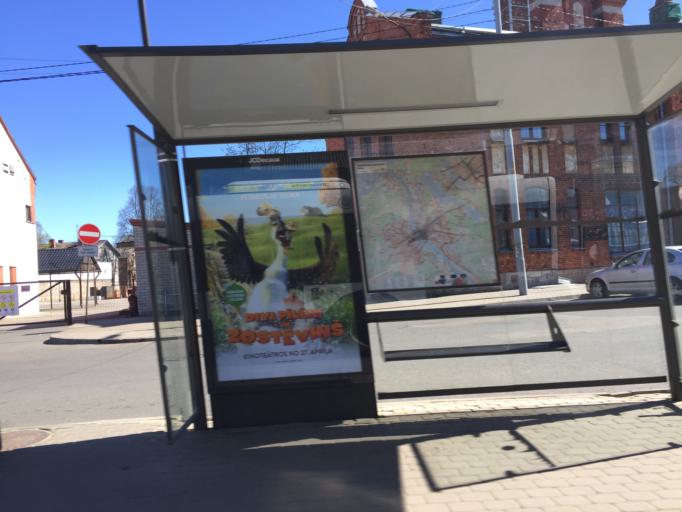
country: LV
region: Riga
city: Riga
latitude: 56.9358
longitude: 24.0711
